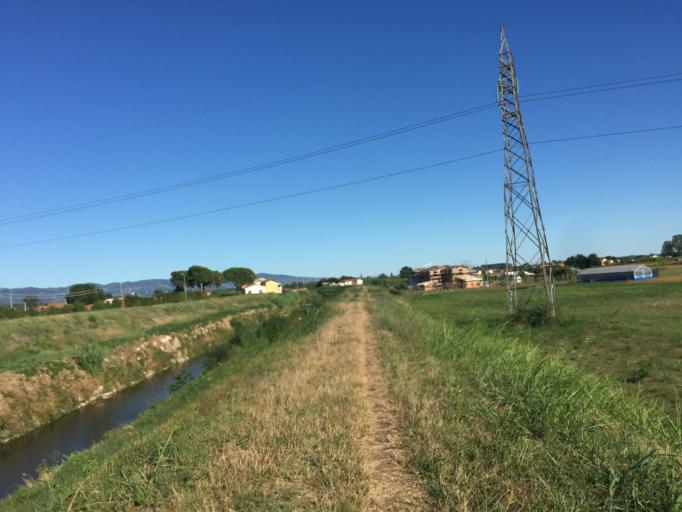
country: IT
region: Tuscany
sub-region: Provincia di Pistoia
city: Ponte Buggianese
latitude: 43.8371
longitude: 10.7544
